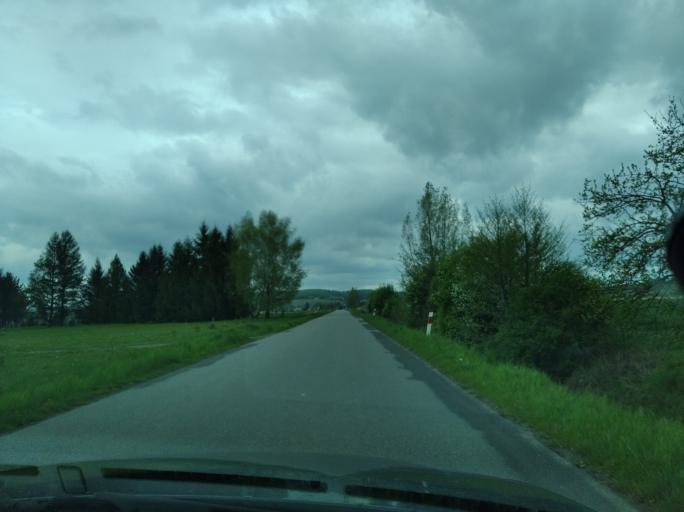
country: PL
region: Subcarpathian Voivodeship
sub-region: Powiat sanocki
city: Dlugie
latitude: 49.5939
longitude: 22.0493
